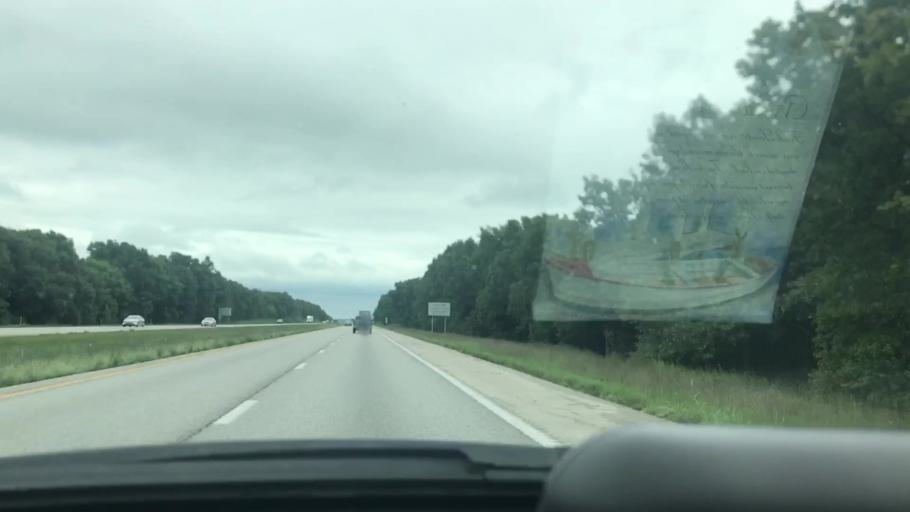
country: US
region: Missouri
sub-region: Lawrence County
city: Mount Vernon
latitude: 37.1412
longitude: -93.7189
